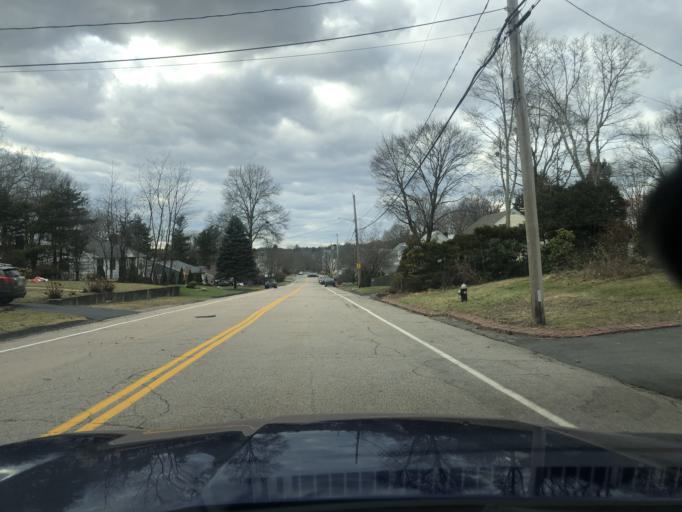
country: US
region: Massachusetts
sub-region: Plymouth County
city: Brockton
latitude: 42.1072
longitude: -71.0109
